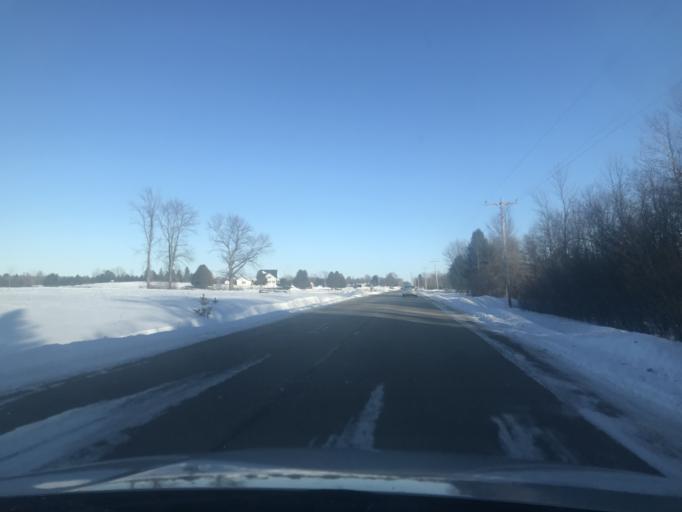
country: US
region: Wisconsin
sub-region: Marinette County
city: Marinette
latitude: 45.1451
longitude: -87.6646
